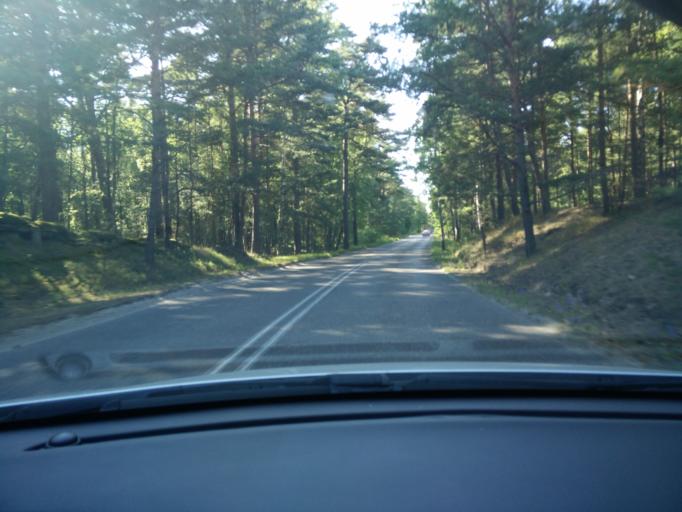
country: PL
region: Pomeranian Voivodeship
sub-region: Powiat pucki
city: Hel
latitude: 54.6285
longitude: 18.7898
